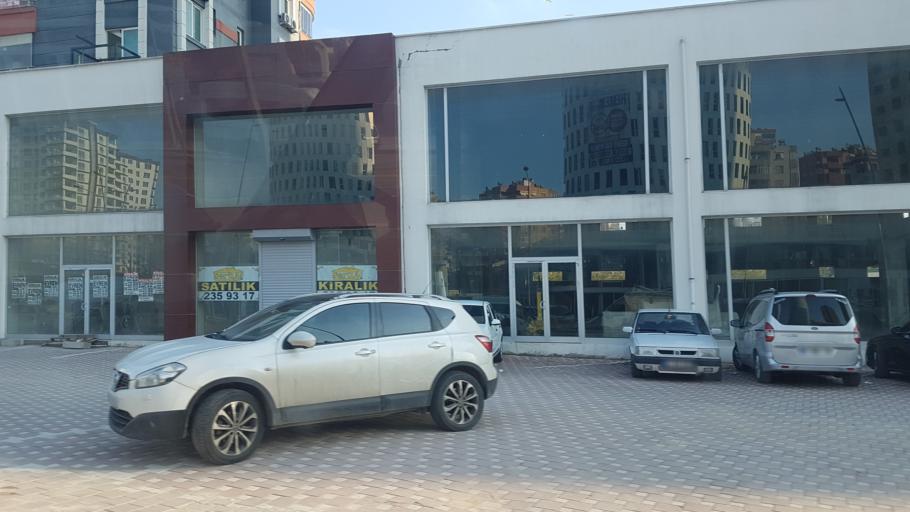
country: TR
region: Adana
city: Seyhan
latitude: 37.0329
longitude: 35.2879
